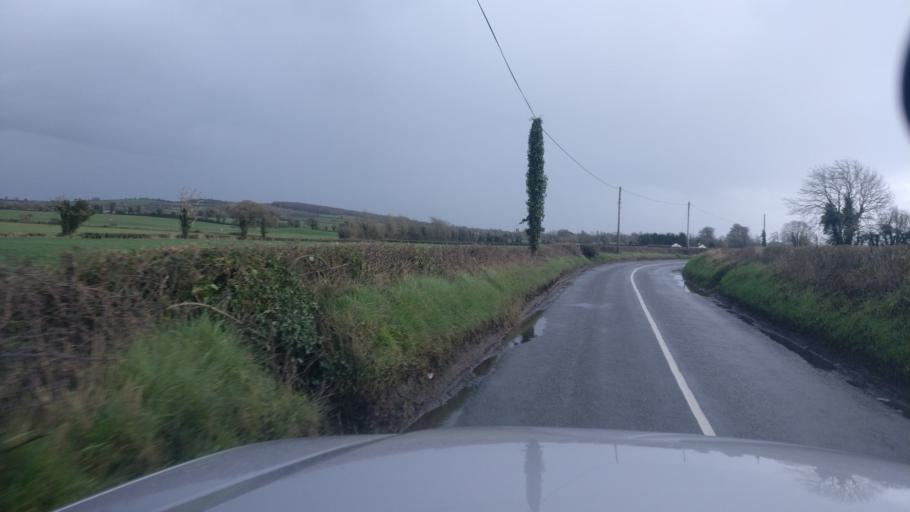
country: IE
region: Munster
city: Nenagh Bridge
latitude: 52.9603
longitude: -8.0812
